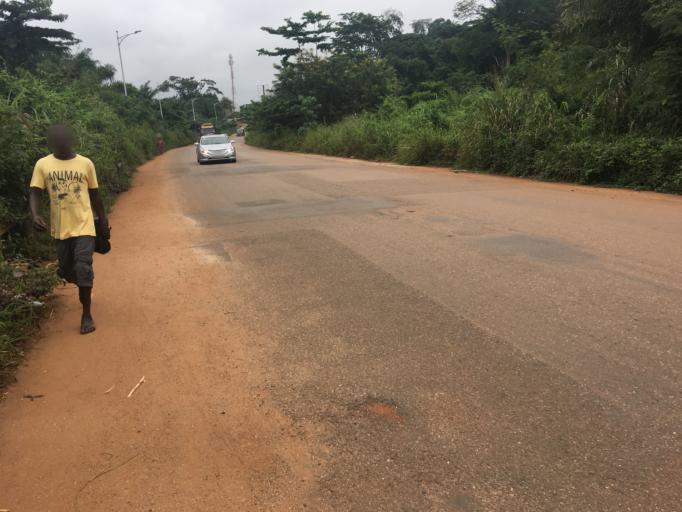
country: GH
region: Western
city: Bibiani
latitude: 6.8077
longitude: -2.5098
